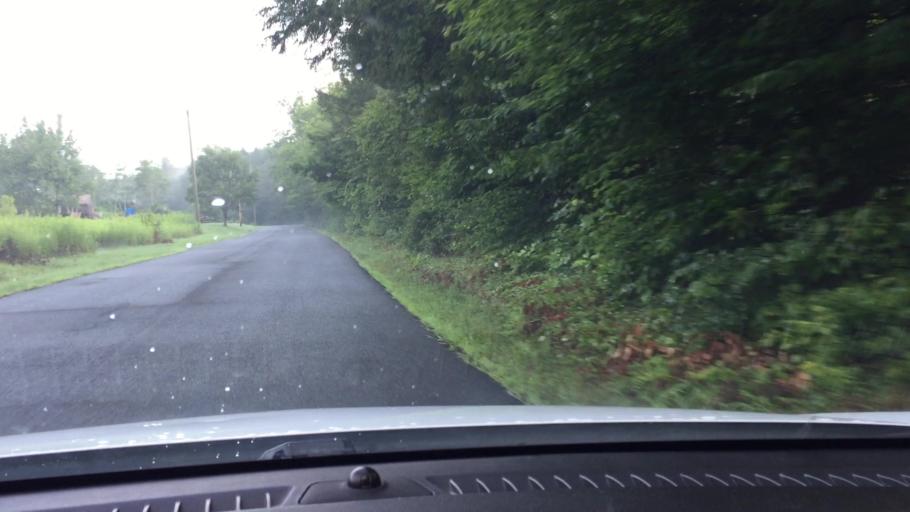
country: US
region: Massachusetts
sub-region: Berkshire County
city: Becket
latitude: 42.3554
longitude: -72.9638
